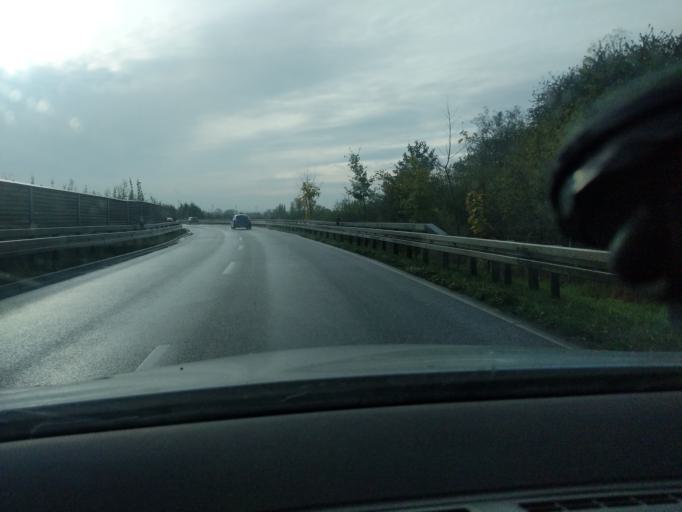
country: DE
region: Lower Saxony
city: Neu Wulmstorf
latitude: 53.5188
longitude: 9.8283
